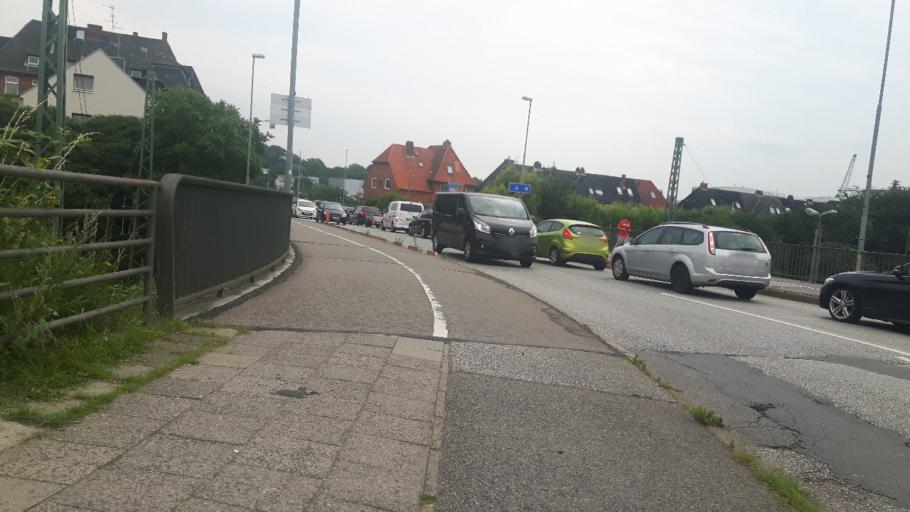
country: DE
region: Schleswig-Holstein
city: Luebeck
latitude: 53.8844
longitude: 10.6878
